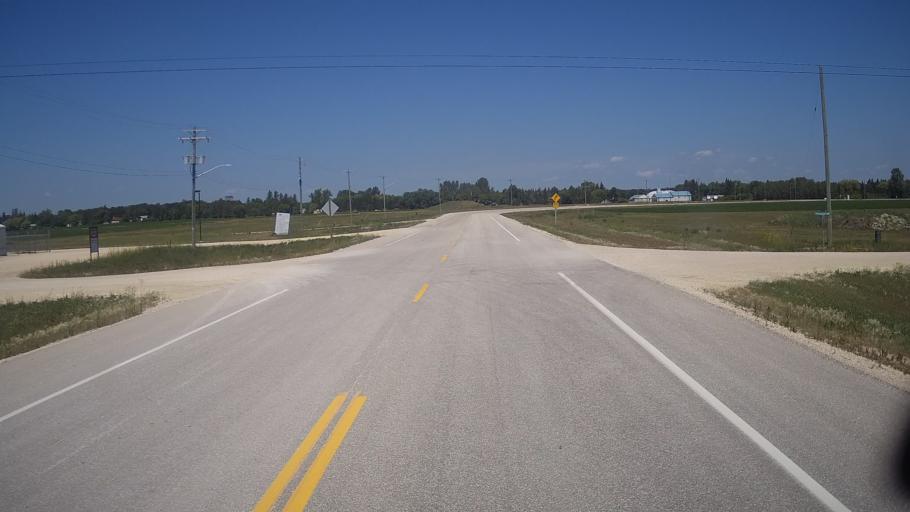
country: CA
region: Manitoba
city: Stonewall
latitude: 50.1240
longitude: -97.5443
